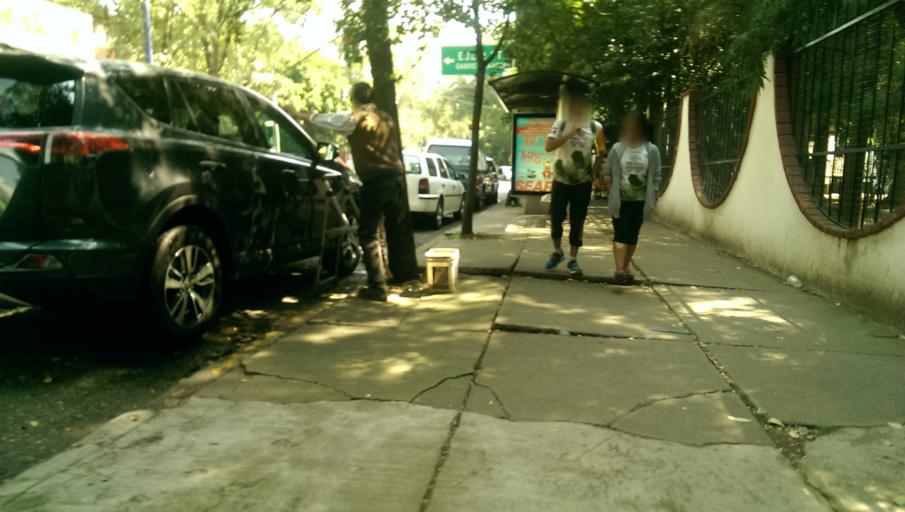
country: MX
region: Mexico City
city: Coyoacan
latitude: 19.3565
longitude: -99.1694
